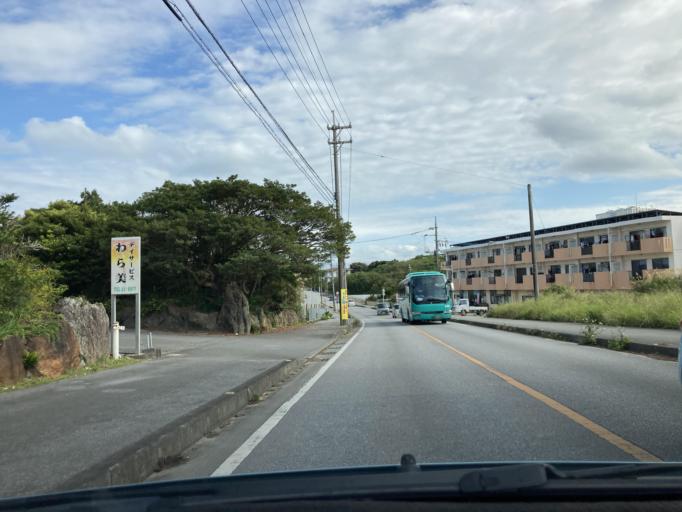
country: JP
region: Okinawa
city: Nago
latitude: 26.6938
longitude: 127.9547
